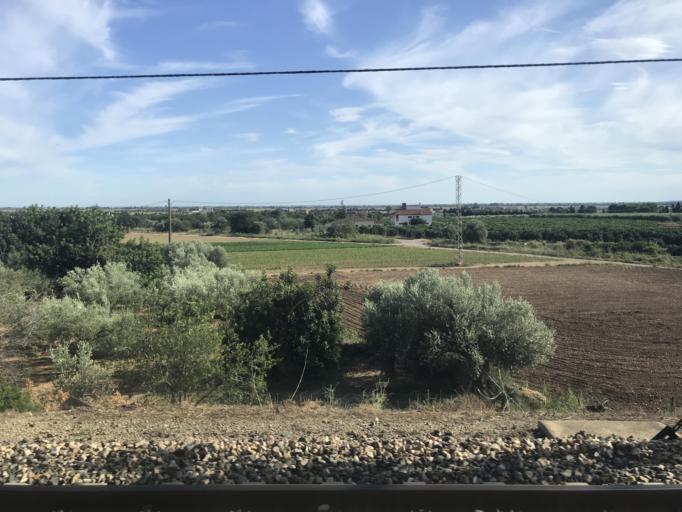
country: ES
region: Catalonia
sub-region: Provincia de Tarragona
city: Amposta
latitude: 40.7509
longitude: 0.6068
